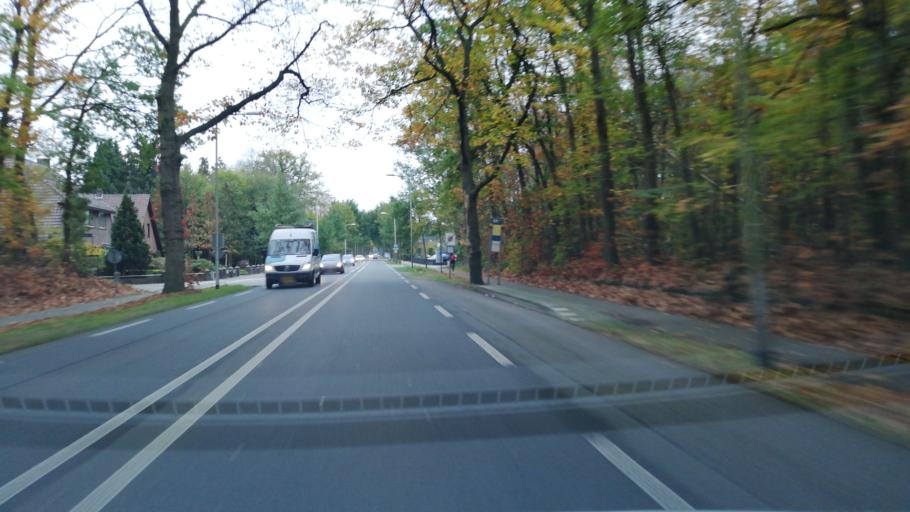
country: NL
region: Gelderland
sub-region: Gemeente Apeldoorn
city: Beekbergen
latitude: 52.1703
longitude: 5.9621
